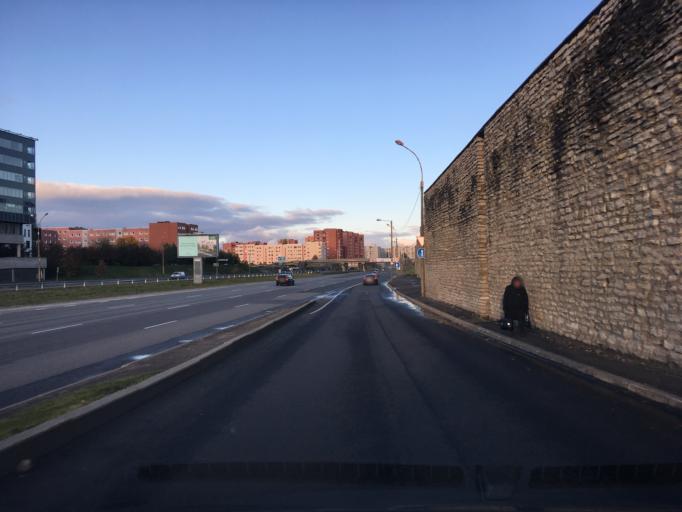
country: EE
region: Harju
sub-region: Tallinna linn
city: Tallinn
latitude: 59.4370
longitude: 24.8132
